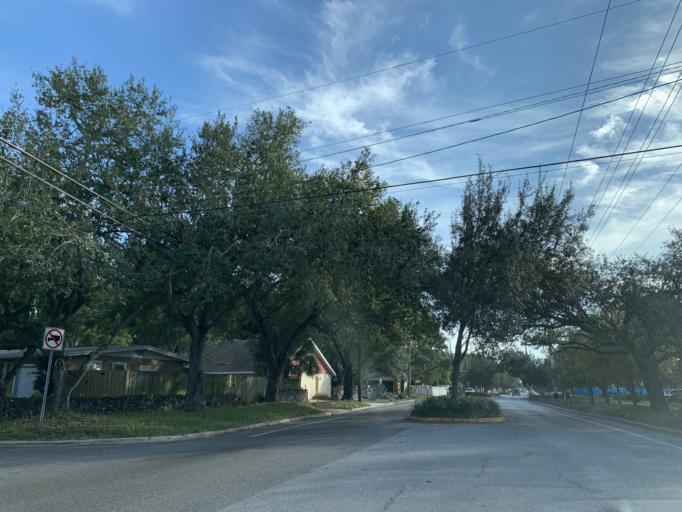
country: US
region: Florida
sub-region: Hillsborough County
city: Tampa
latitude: 27.9008
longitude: -82.5022
